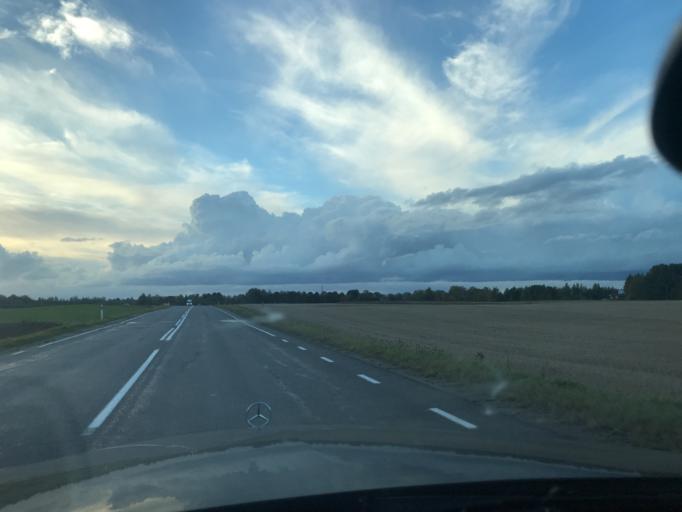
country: EE
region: Vorumaa
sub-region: Antsla vald
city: Vana-Antsla
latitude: 57.8880
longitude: 26.5145
